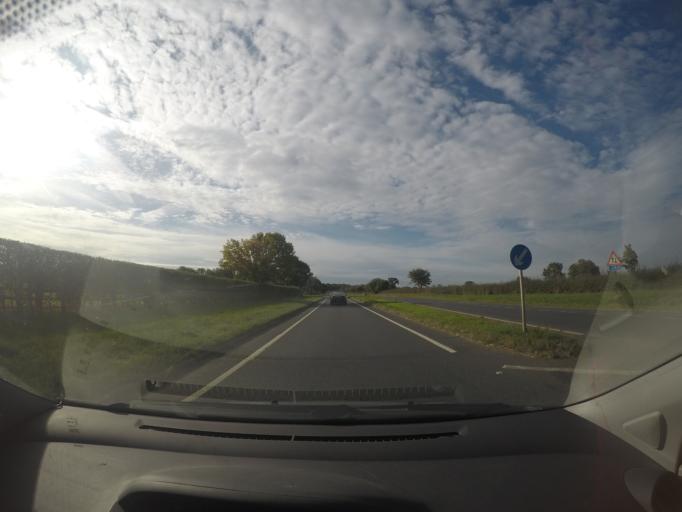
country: GB
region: England
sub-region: City of York
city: Deighton
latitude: 53.8864
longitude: -1.0465
